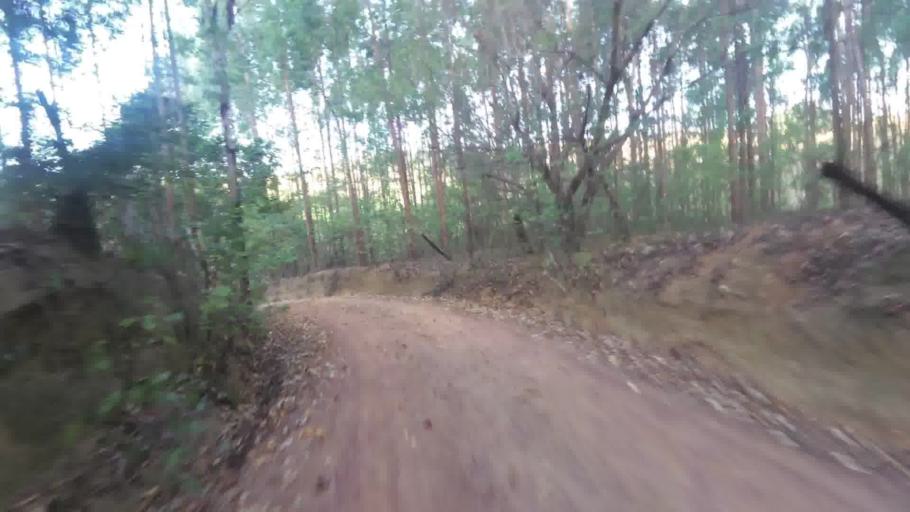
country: BR
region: Espirito Santo
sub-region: Marataizes
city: Marataizes
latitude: -21.1627
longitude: -41.0386
